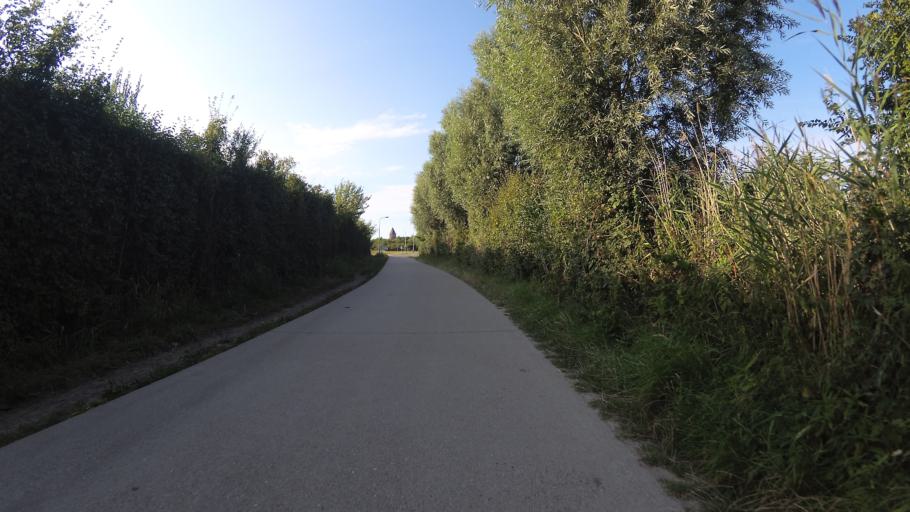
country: NL
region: Zeeland
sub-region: Gemeente Middelburg
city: Middelburg
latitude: 51.5666
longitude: 3.5231
